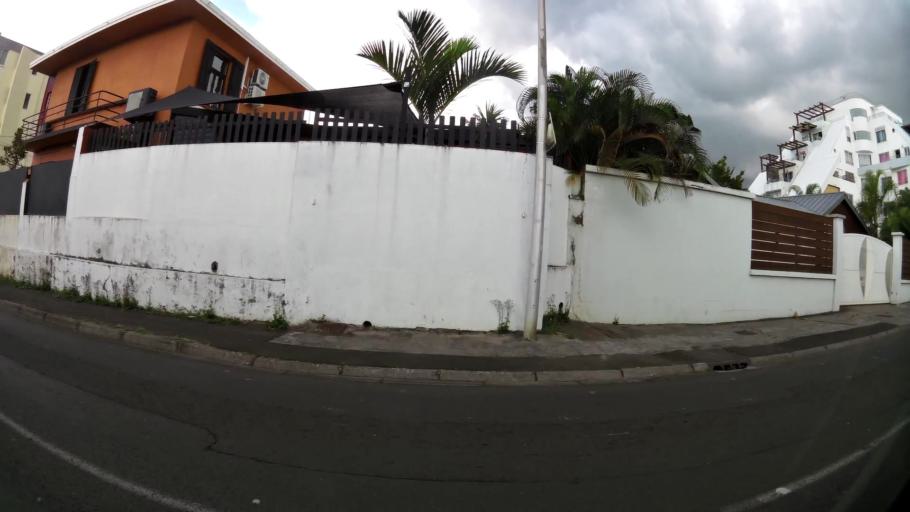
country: RE
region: Reunion
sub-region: Reunion
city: Saint-Denis
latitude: -20.8883
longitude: 55.4586
